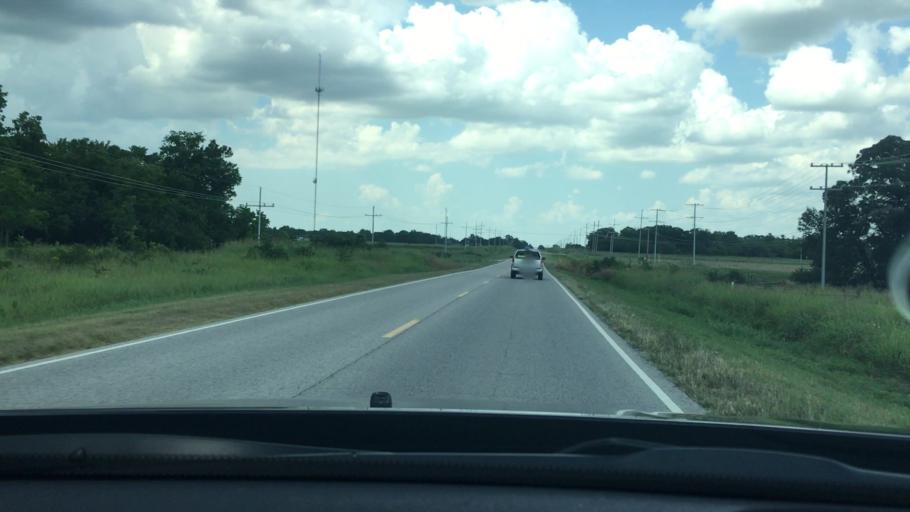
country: US
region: Oklahoma
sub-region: Pontotoc County
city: Ada
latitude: 34.6475
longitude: -96.6349
